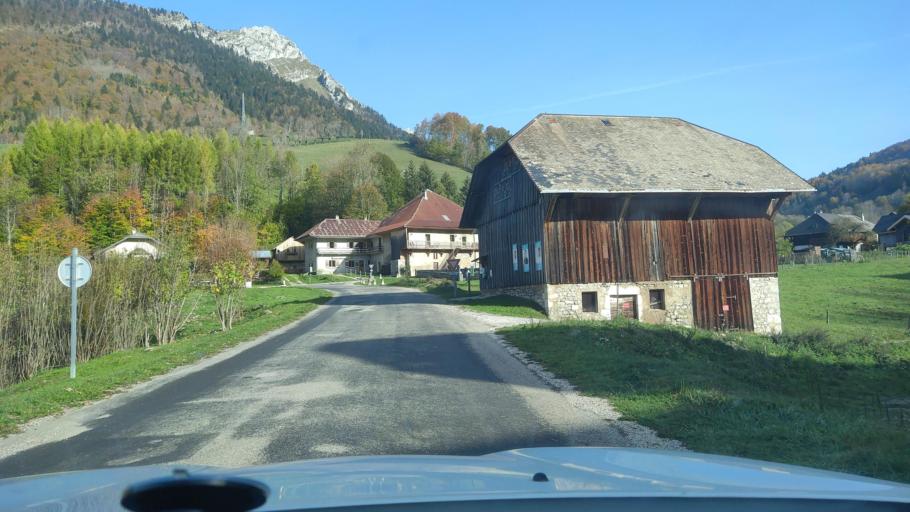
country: FR
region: Rhone-Alpes
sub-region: Departement de la Savoie
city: Cruet
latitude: 45.6090
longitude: 6.1054
